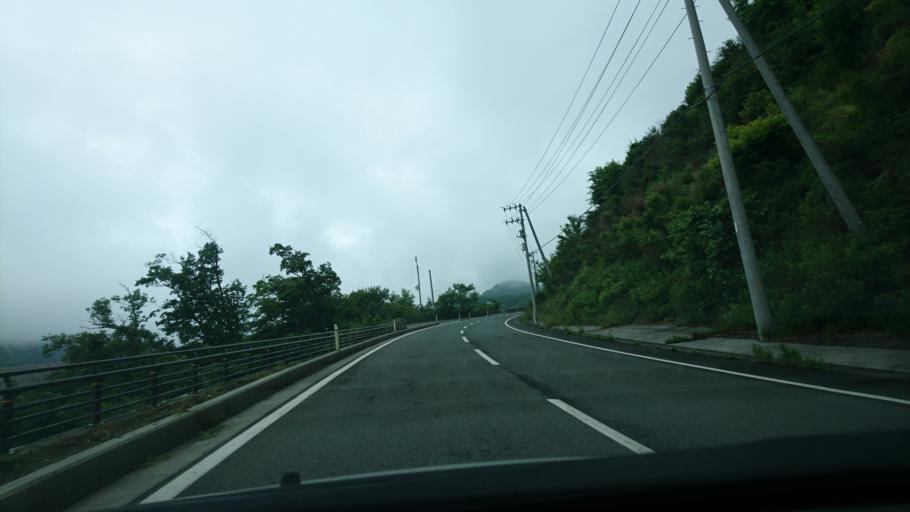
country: JP
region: Iwate
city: Mizusawa
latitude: 39.1248
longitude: 140.9253
